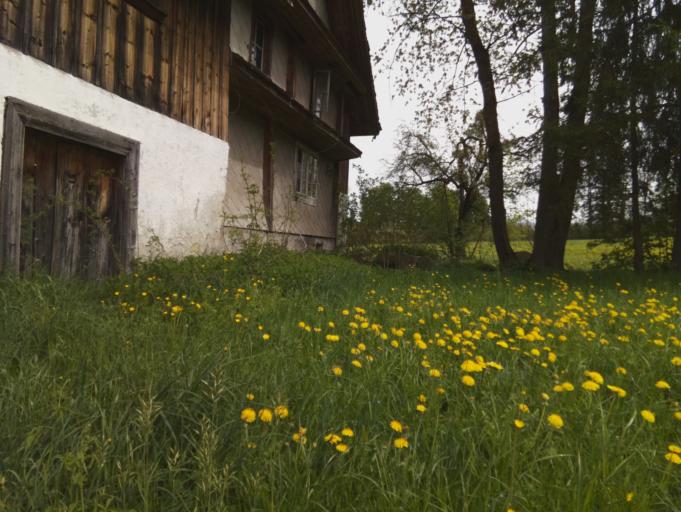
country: CH
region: Schwyz
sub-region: Bezirk March
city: Lachen
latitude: 47.1796
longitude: 8.8537
